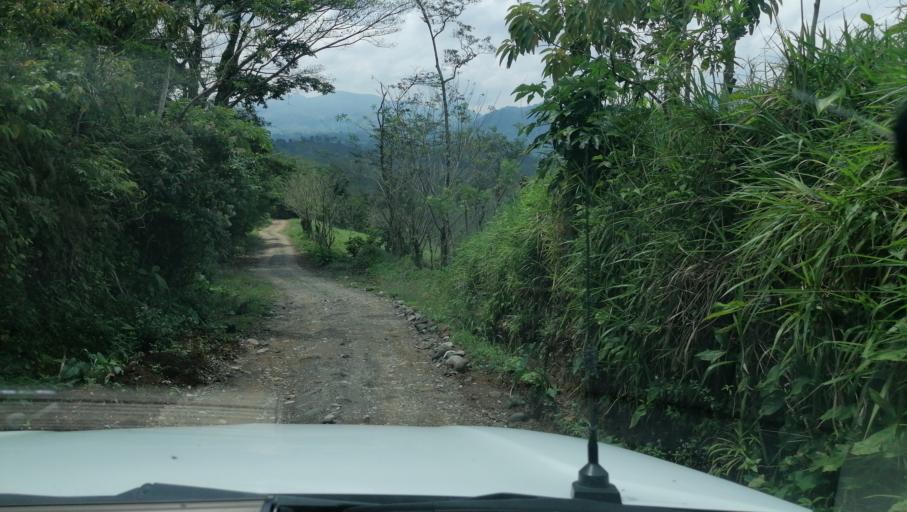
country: MX
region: Chiapas
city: Ixtacomitan
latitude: 17.4467
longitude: -93.2000
